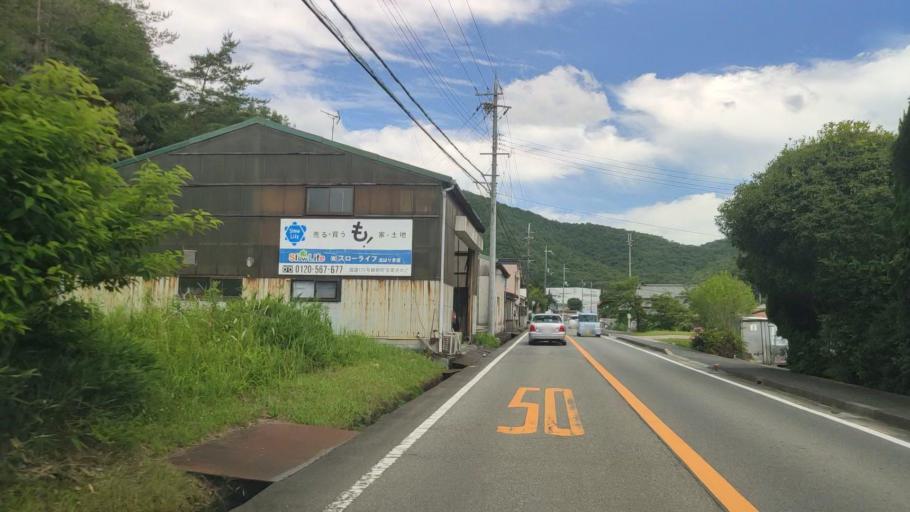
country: JP
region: Hyogo
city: Nishiwaki
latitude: 35.0217
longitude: 134.9471
